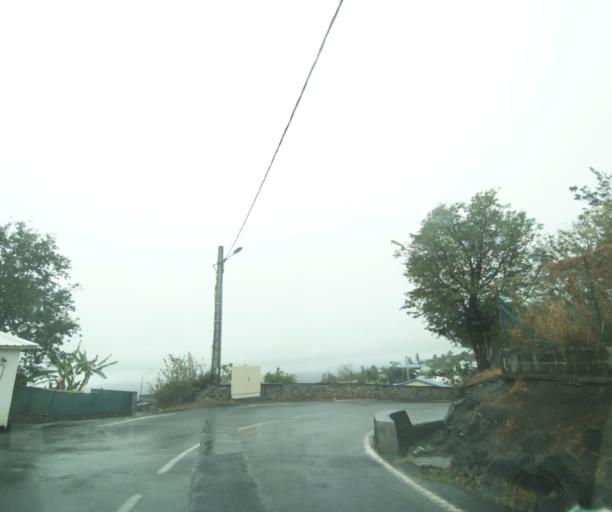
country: RE
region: Reunion
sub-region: Reunion
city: Saint-Paul
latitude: -21.0287
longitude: 55.2852
